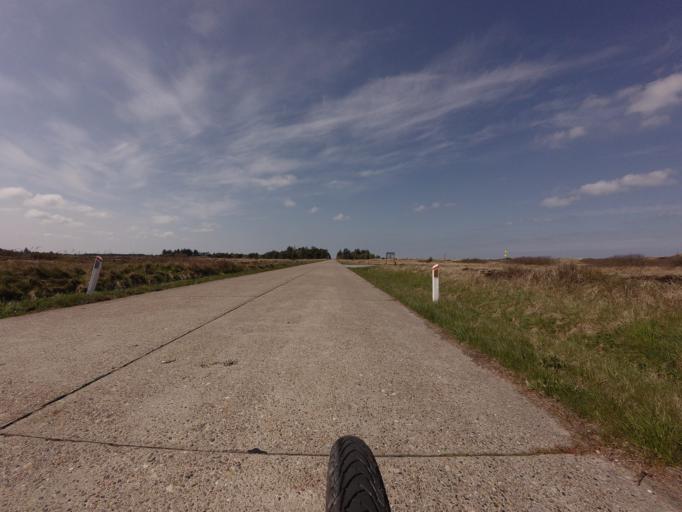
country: DK
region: North Denmark
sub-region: Jammerbugt Kommune
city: Brovst
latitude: 57.1688
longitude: 9.4698
